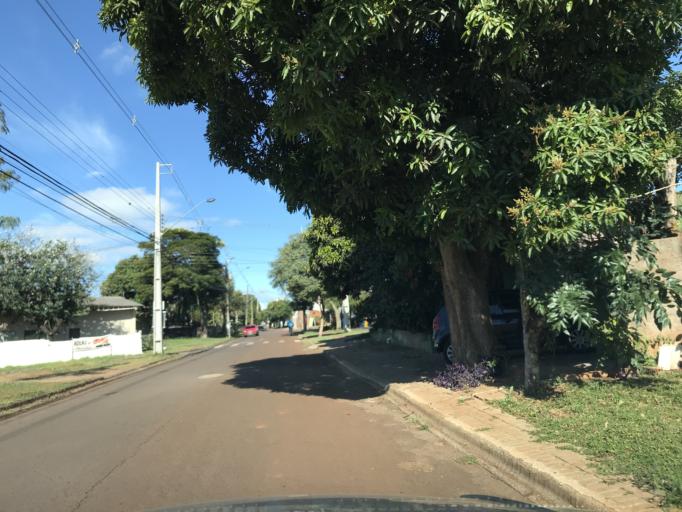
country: BR
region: Parana
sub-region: Cascavel
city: Cascavel
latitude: -24.9380
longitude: -53.4687
